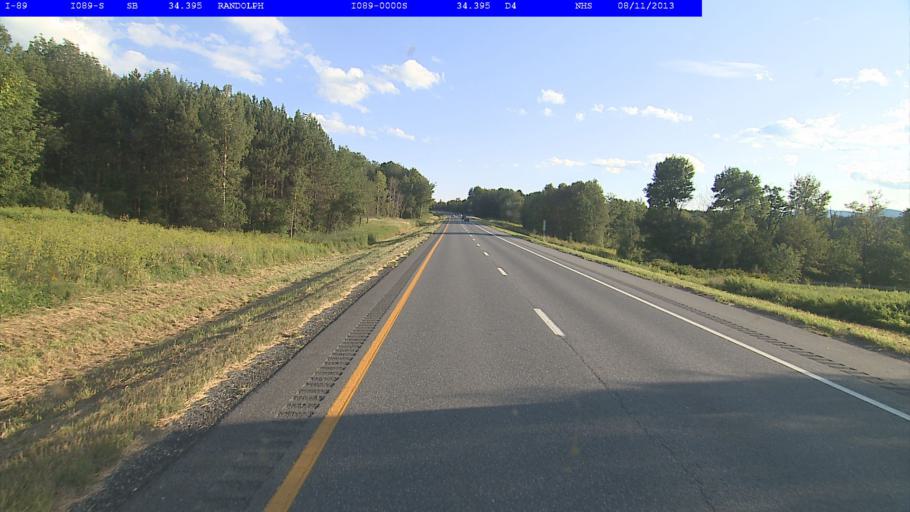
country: US
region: Vermont
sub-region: Orange County
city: Randolph
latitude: 43.9953
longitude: -72.6256
